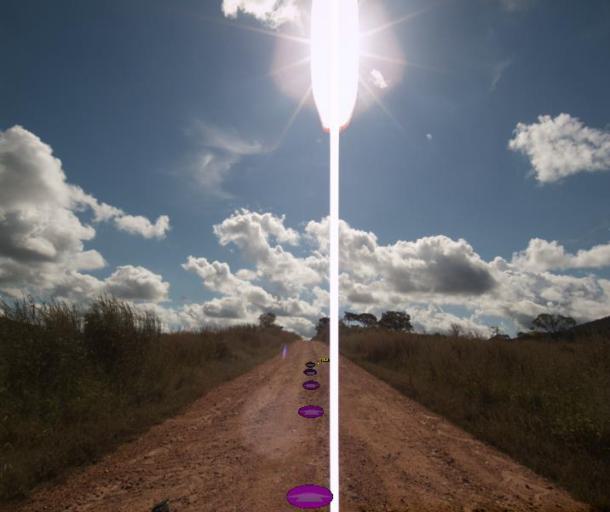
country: BR
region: Goias
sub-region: Jaragua
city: Jaragua
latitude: -15.8202
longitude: -49.1834
